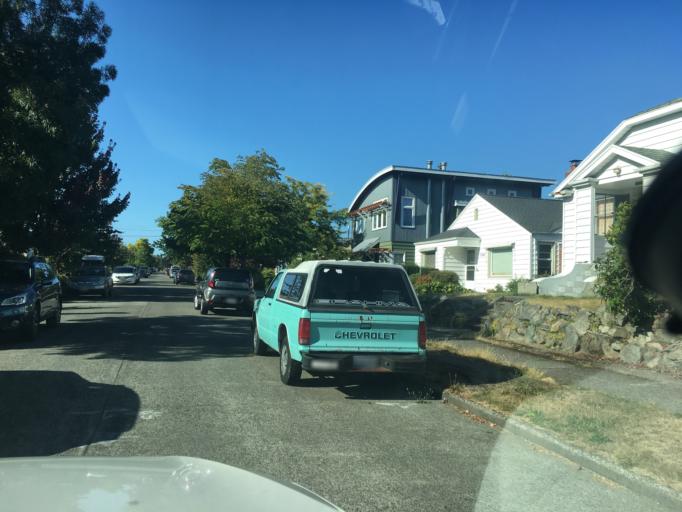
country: US
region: Washington
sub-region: King County
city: Shoreline
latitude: 47.6842
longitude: -122.3865
